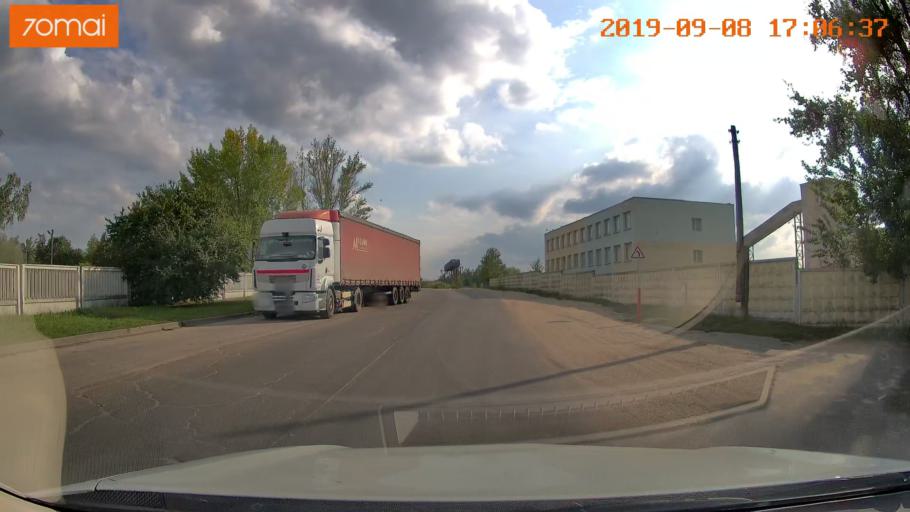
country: BY
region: Grodnenskaya
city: Hrodna
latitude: 53.6691
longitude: 23.9522
